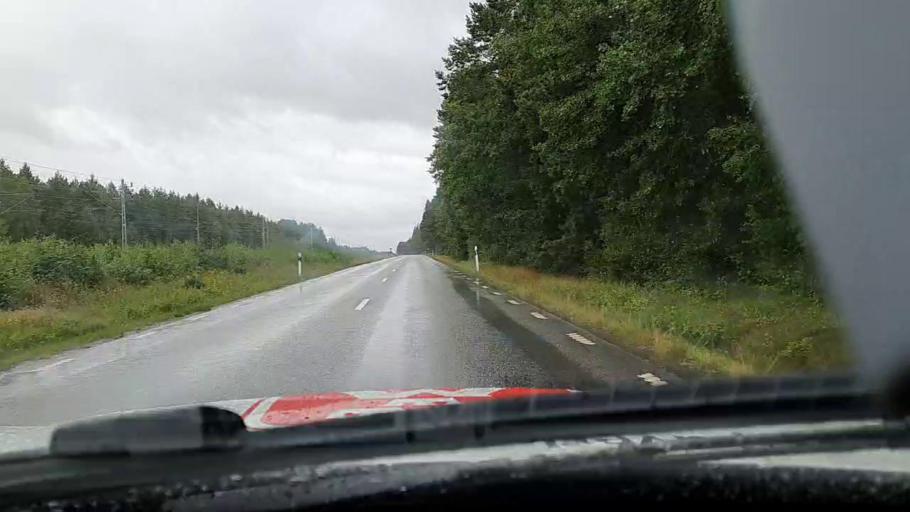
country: SE
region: Vaestra Goetaland
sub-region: Toreboda Kommun
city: Toereboda
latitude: 58.6679
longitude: 14.0937
